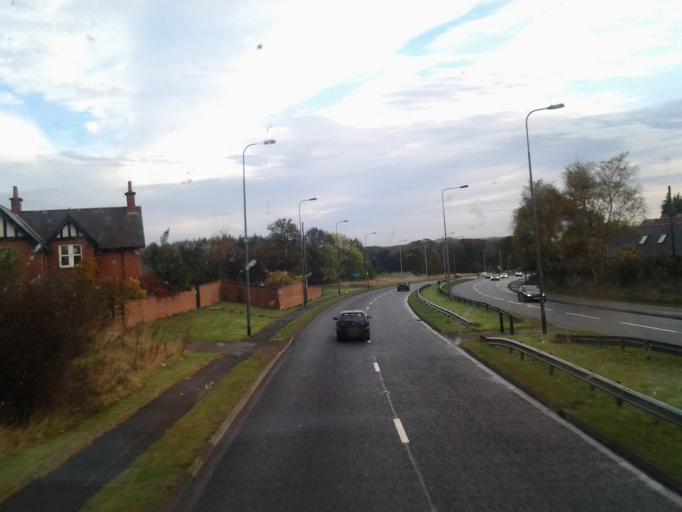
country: GB
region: England
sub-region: County Durham
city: Chester-le-Street
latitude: 54.8393
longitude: -1.5848
